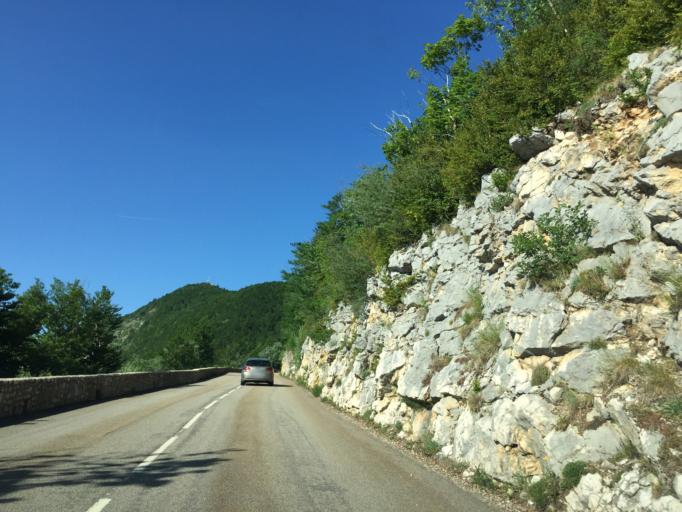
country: FR
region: Rhone-Alpes
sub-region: Departement de la Drome
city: Saint-Laurent-en-Royans
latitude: 44.9087
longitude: 5.3629
